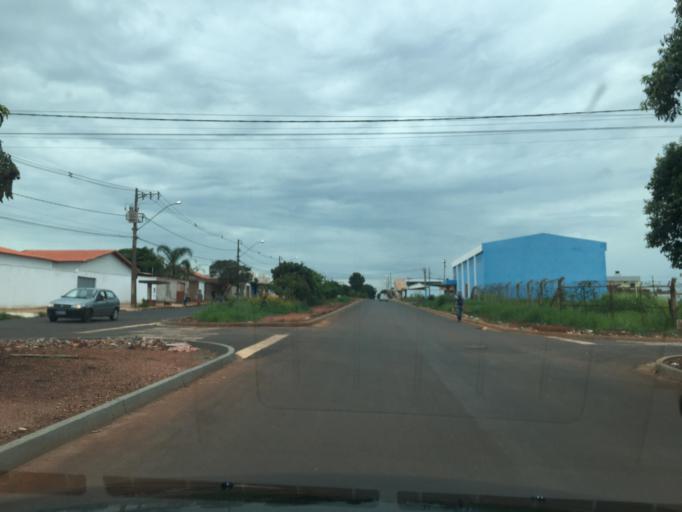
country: BR
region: Minas Gerais
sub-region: Uberlandia
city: Uberlandia
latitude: -18.8704
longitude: -48.2247
